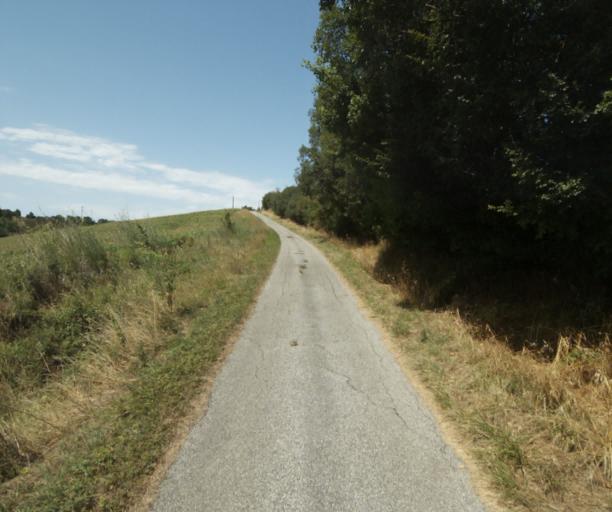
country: FR
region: Midi-Pyrenees
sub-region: Departement de la Haute-Garonne
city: Saint-Felix-Lauragais
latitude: 43.4628
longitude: 1.8627
